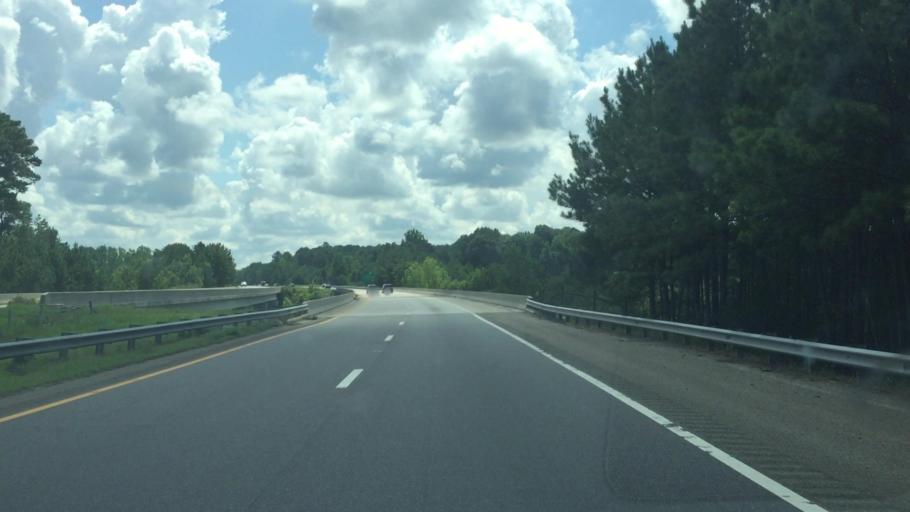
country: US
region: North Carolina
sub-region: Richmond County
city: Cordova
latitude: 34.9219
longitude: -79.8145
